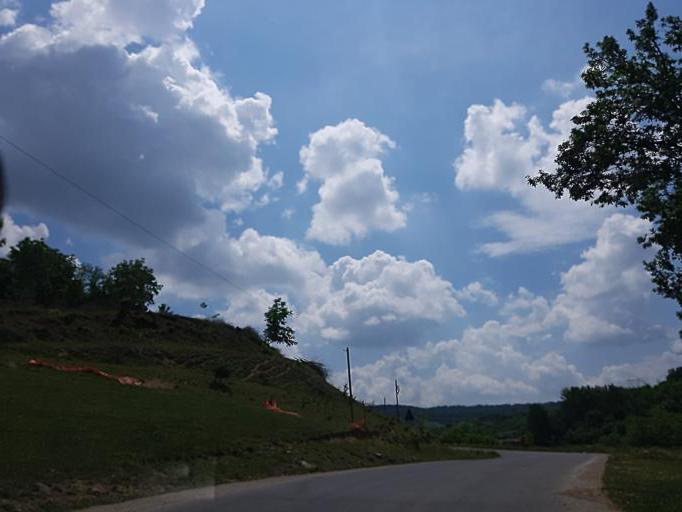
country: RO
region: Sibiu
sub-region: Comuna Seica Mica
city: Seica Mica
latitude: 46.0511
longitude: 24.1457
